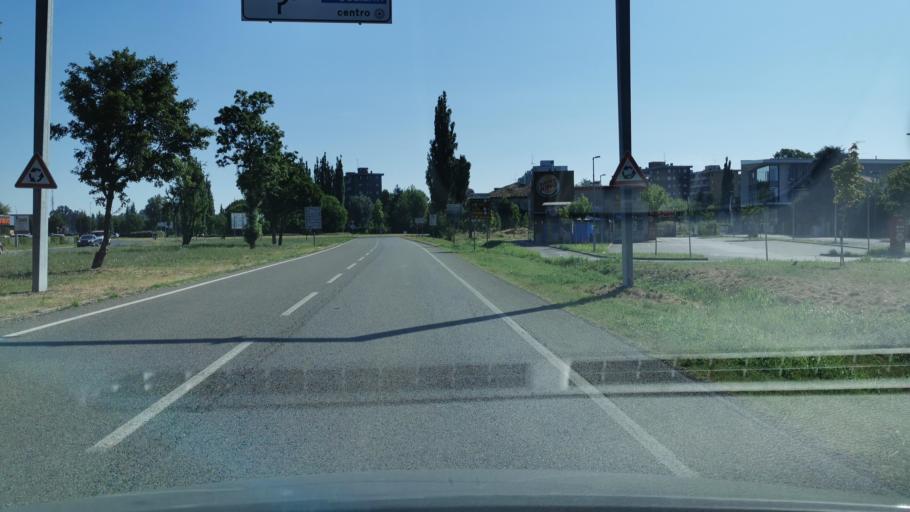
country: IT
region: Emilia-Romagna
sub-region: Provincia di Modena
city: Santa Croce Scuole
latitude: 44.7748
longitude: 10.8611
